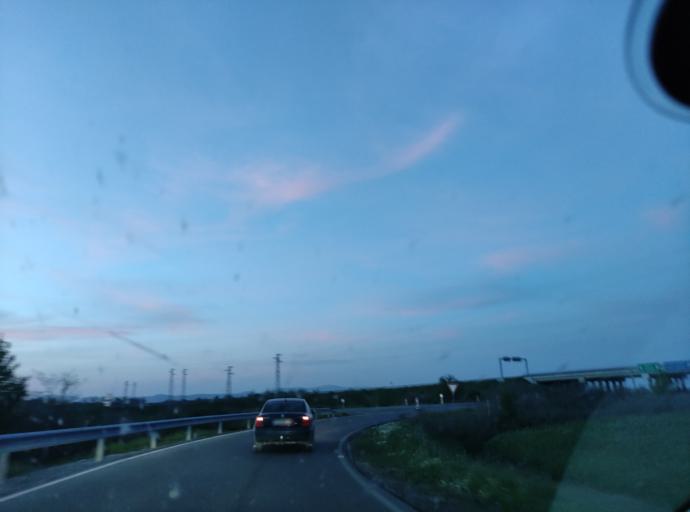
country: BG
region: Stara Zagora
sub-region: Obshtina Stara Zagora
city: Stara Zagora
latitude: 42.3383
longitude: 25.6603
